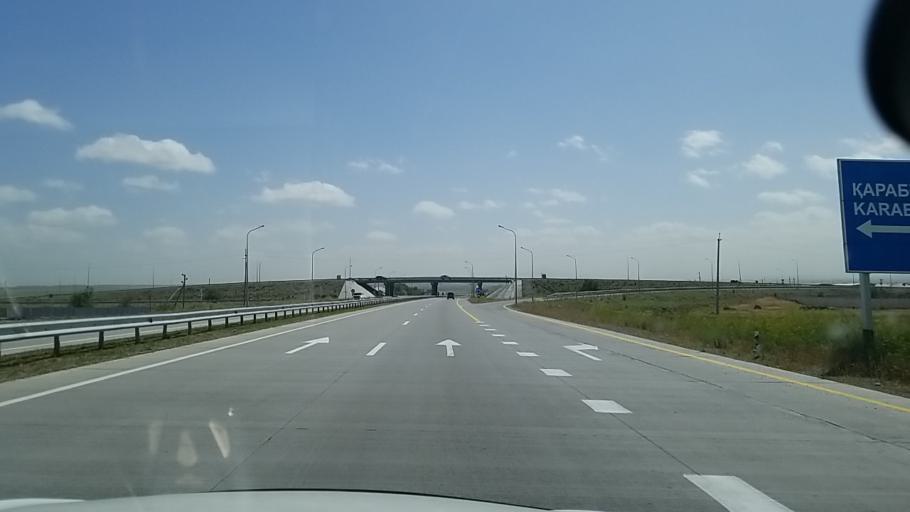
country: KZ
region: Ongtustik Qazaqstan
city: Aksu
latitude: 42.4727
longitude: 69.8116
